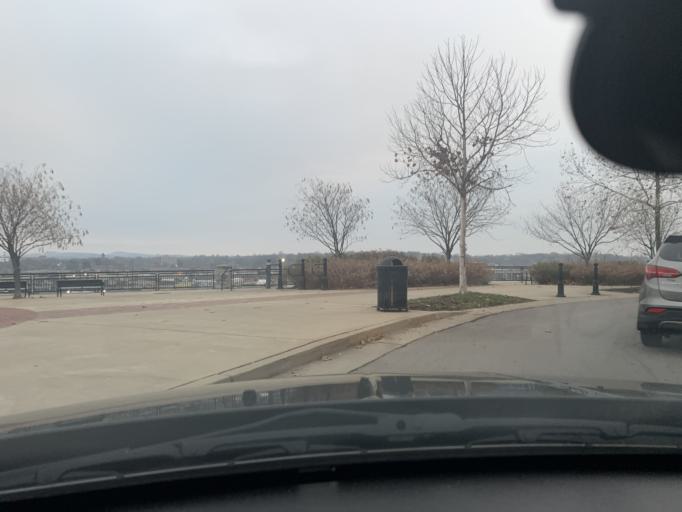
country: US
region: Tennessee
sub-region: Davidson County
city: Nashville
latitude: 36.1575
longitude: -86.7665
